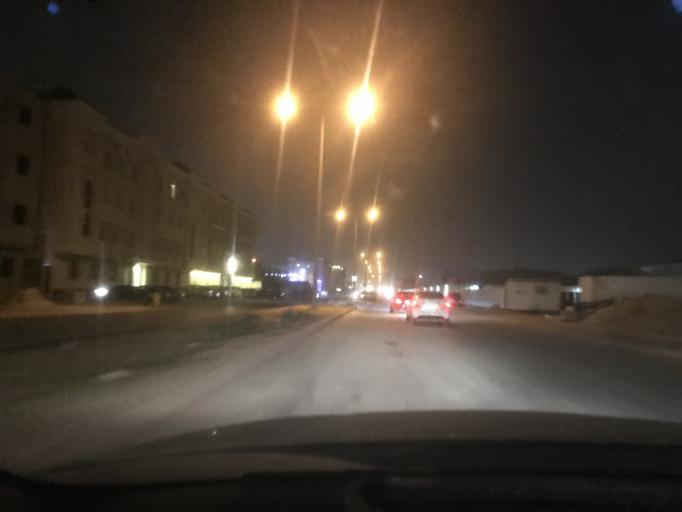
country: SA
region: Ar Riyad
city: Riyadh
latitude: 24.8279
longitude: 46.7356
